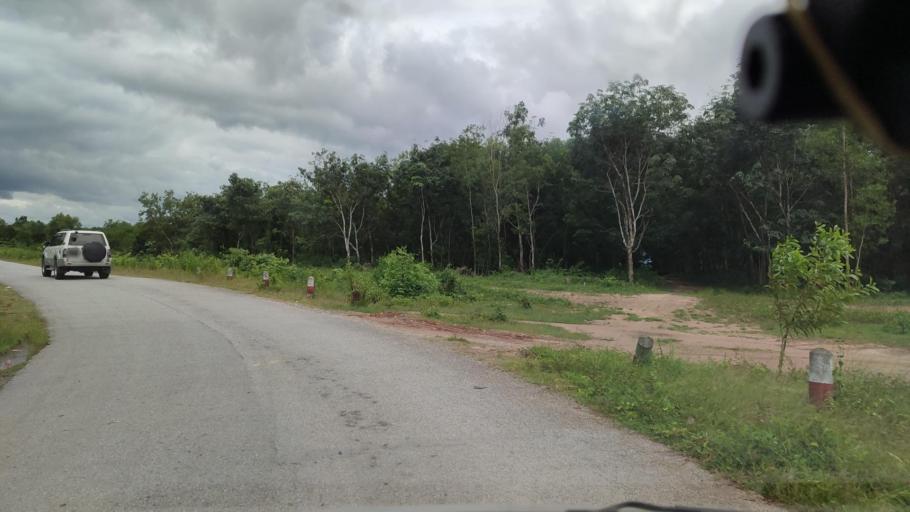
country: MM
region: Bago
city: Thanatpin
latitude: 17.2518
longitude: 96.3834
